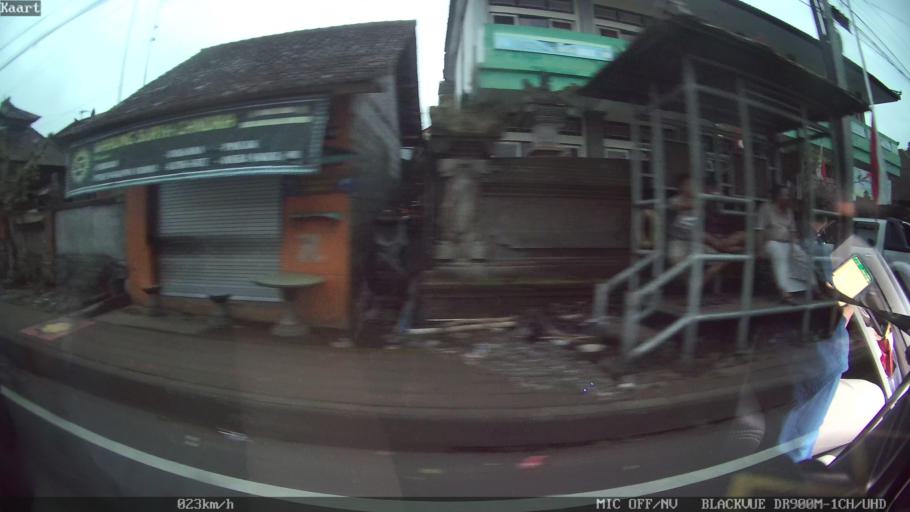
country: ID
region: Bali
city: Badung
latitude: -8.4301
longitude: 115.2457
